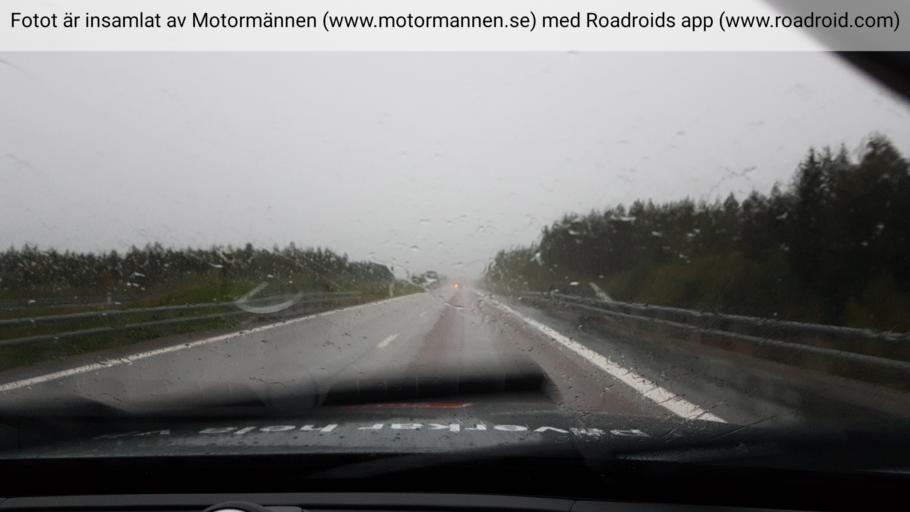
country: SE
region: Uppsala
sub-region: Tierps Kommun
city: Tierp
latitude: 60.2495
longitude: 17.5003
